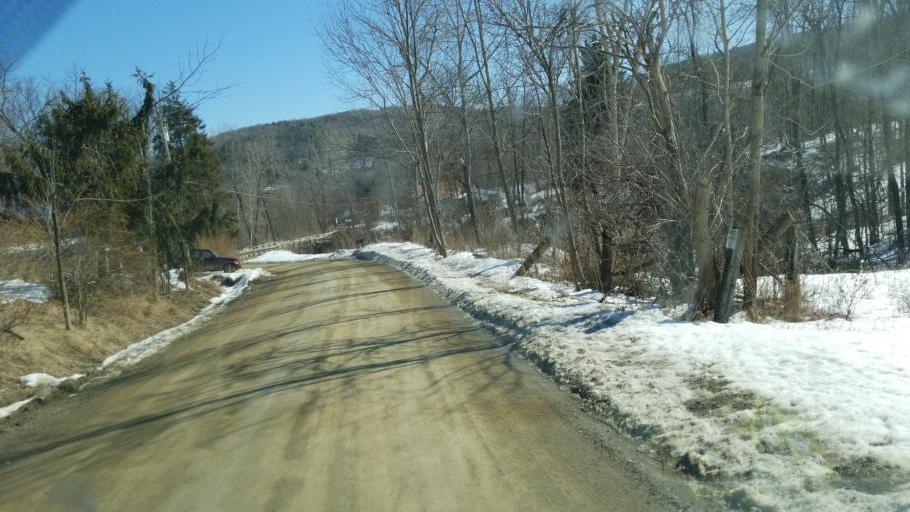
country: US
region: New York
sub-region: Steuben County
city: Hornell
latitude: 42.2478
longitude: -77.6986
